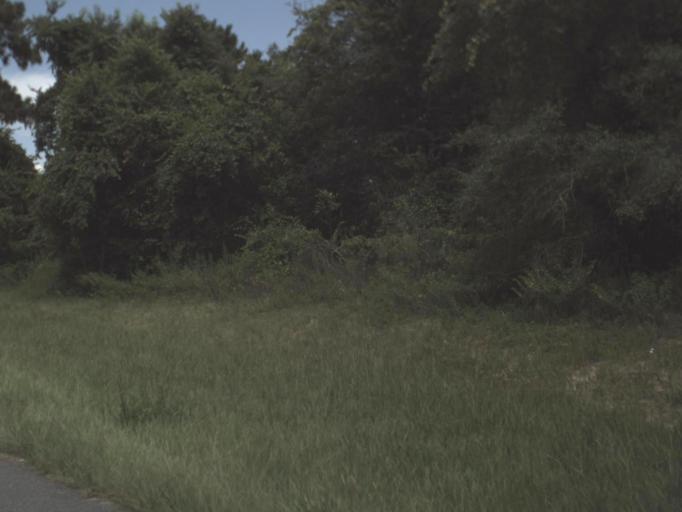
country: US
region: Florida
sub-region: Citrus County
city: Hernando
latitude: 28.9788
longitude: -82.3596
